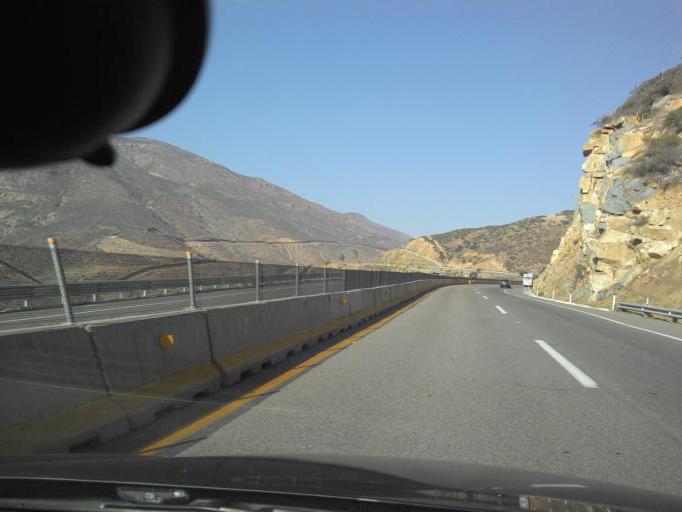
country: MX
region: Baja California
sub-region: Tijuana
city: Ejido Javier Rojo Gomez
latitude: 32.5524
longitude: -116.8346
